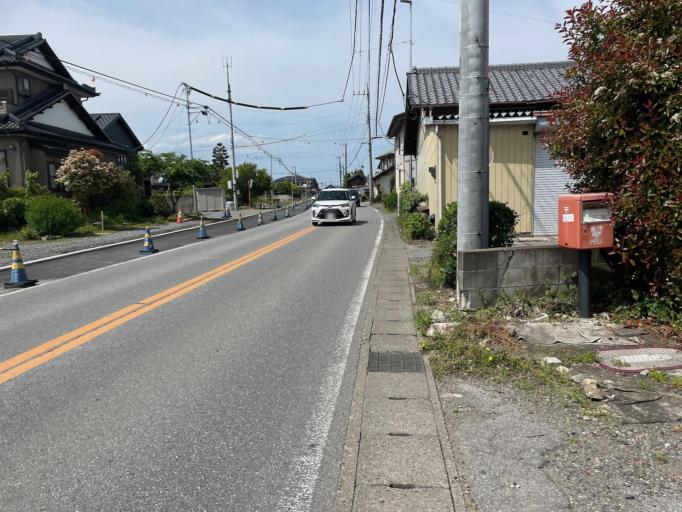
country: JP
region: Tochigi
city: Mibu
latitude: 36.4744
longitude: 139.7646
